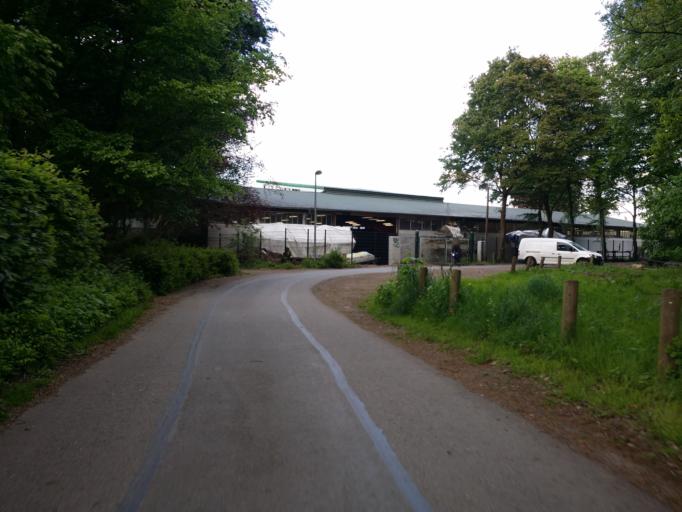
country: DE
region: Bremen
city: Bremen
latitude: 53.0671
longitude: 8.8180
